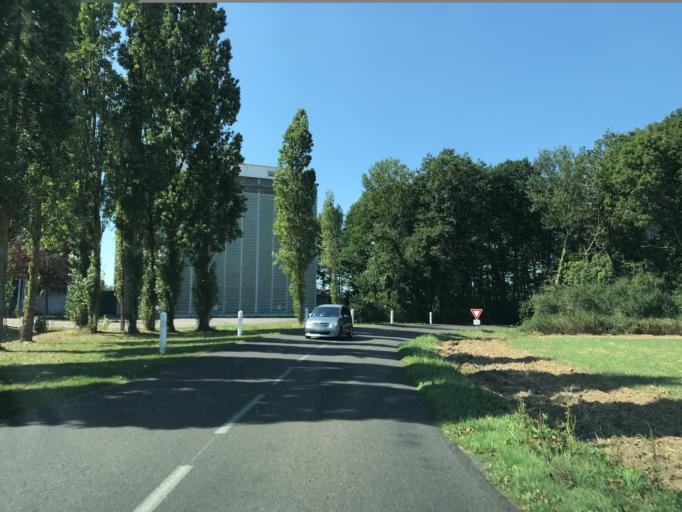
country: FR
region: Haute-Normandie
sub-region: Departement de l'Eure
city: Houlbec-Cocherel
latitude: 49.0938
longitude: 1.3522
